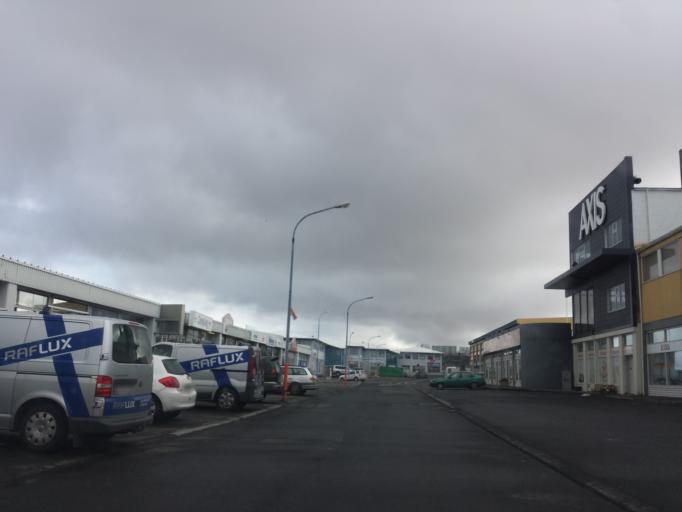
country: IS
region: Capital Region
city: Reykjavik
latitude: 64.1129
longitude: -21.8508
